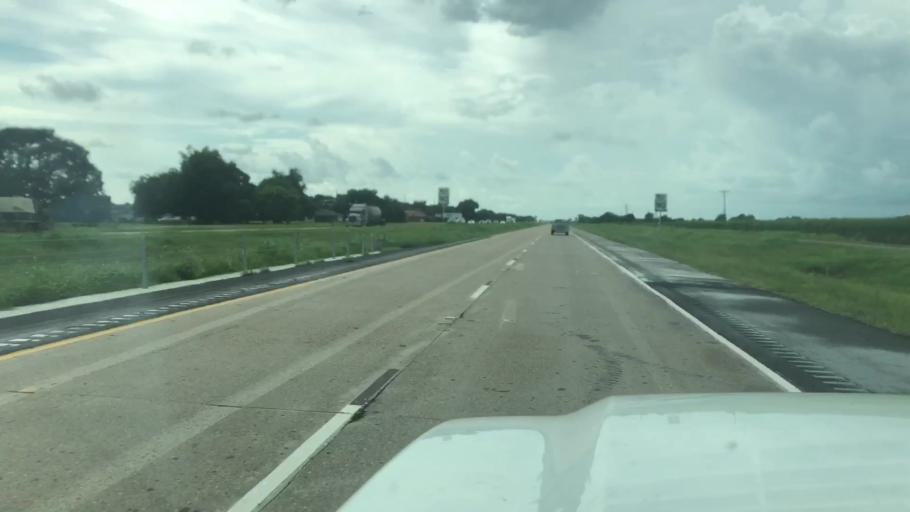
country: US
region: Louisiana
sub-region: Iberia Parish
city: Jeanerette
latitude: 29.8712
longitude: -91.6426
